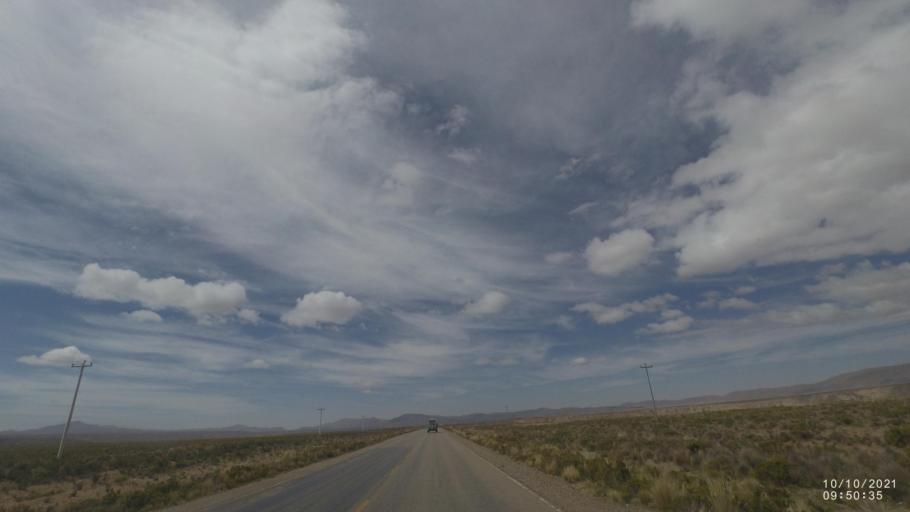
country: BO
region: La Paz
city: Colquiri
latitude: -17.2457
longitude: -67.3330
